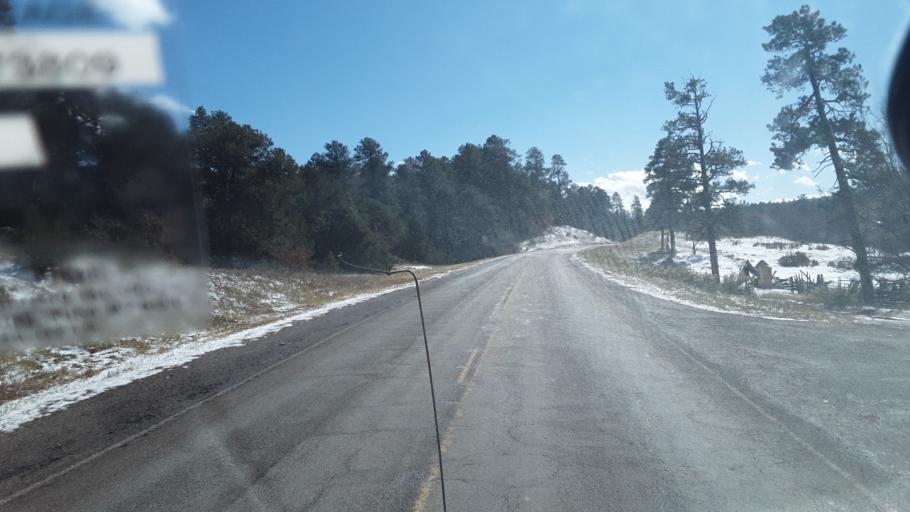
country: US
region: New Mexico
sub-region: Rio Arriba County
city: Santa Teresa
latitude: 36.2109
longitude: -106.7768
